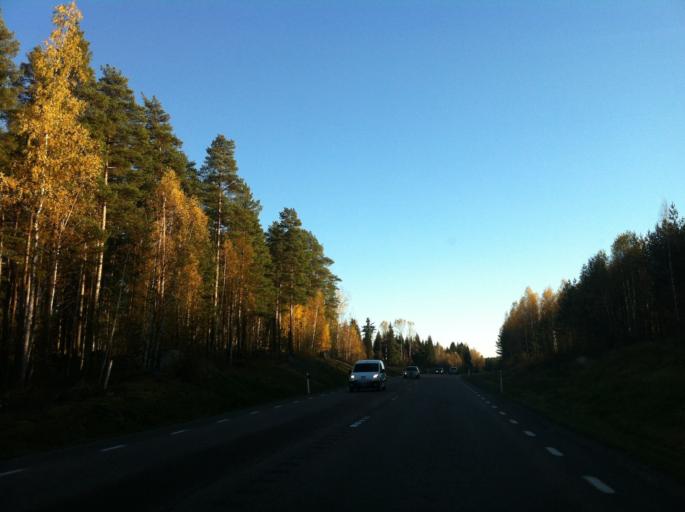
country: SE
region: Dalarna
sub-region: Faluns Kommun
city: Grycksbo
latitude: 60.6599
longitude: 15.5504
